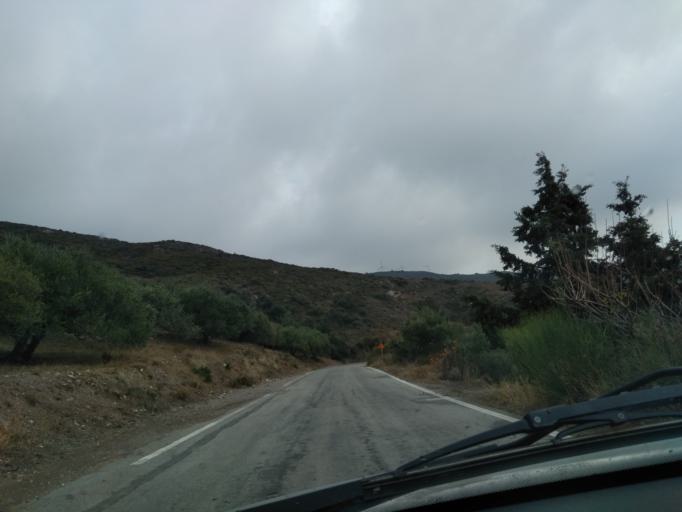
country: GR
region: Crete
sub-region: Nomos Lasithiou
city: Siteia
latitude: 35.1473
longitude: 26.0206
